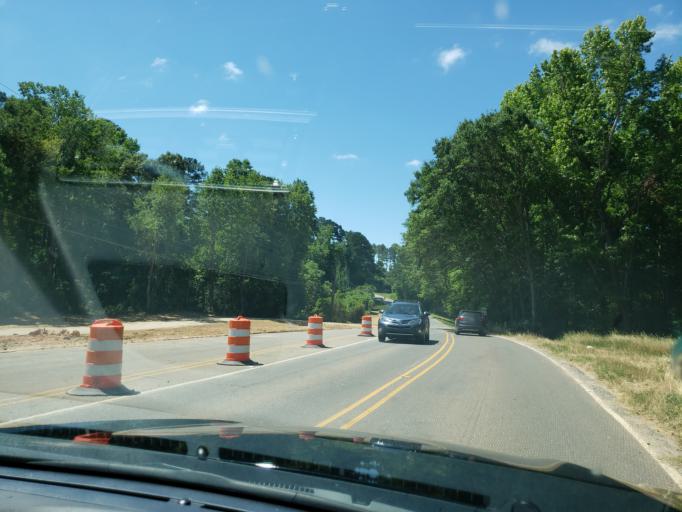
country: US
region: Alabama
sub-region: Lee County
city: Auburn
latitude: 32.6650
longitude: -85.4904
